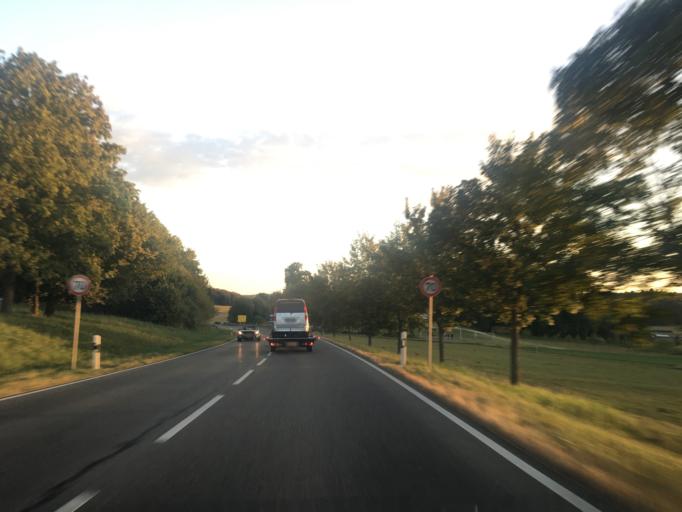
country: DE
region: Baden-Wuerttemberg
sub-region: Tuebingen Region
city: Gomadingen
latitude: 48.3599
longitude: 9.3278
